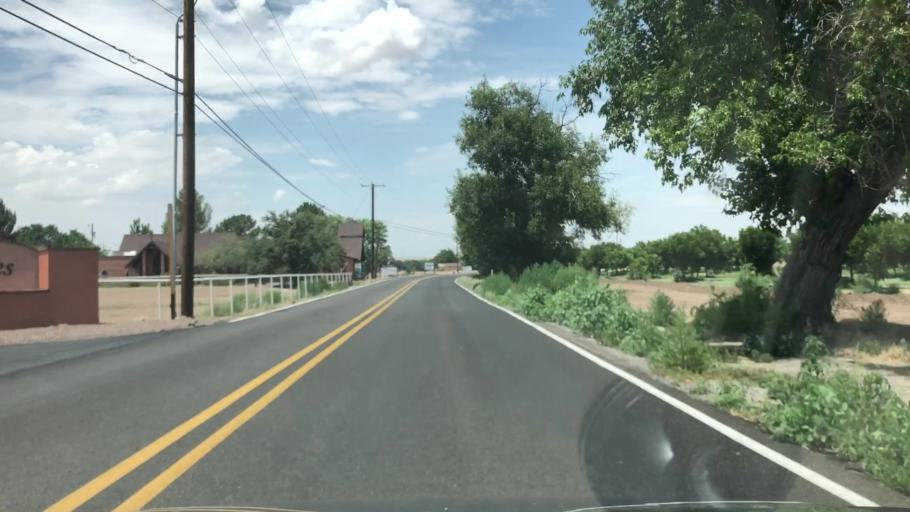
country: US
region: Texas
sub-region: El Paso County
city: Canutillo
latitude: 31.9193
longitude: -106.6307
